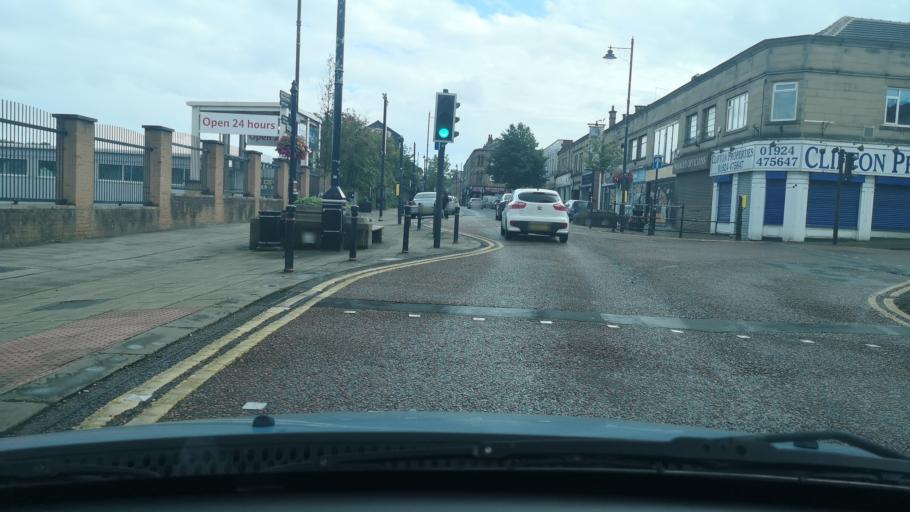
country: GB
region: England
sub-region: Kirklees
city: Batley
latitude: 53.7137
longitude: -1.6316
